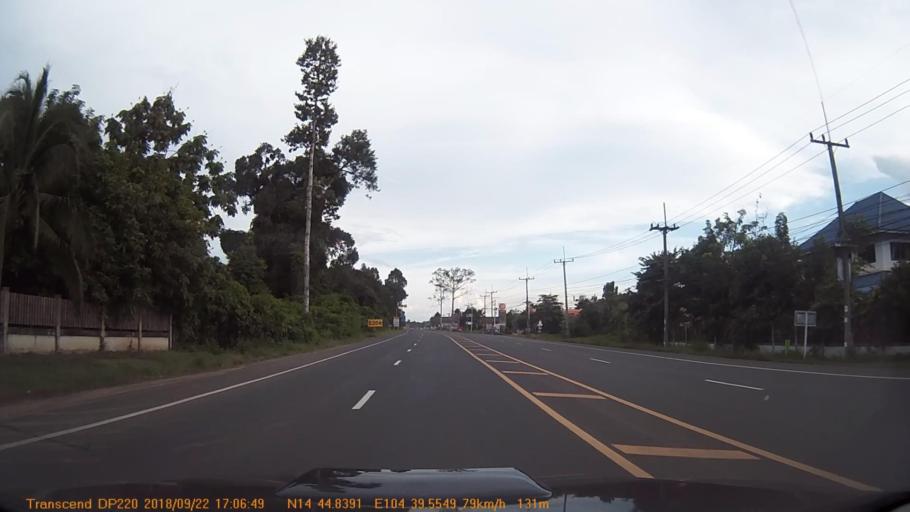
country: TH
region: Sisaket
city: Benchalak
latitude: 14.7475
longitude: 104.6592
